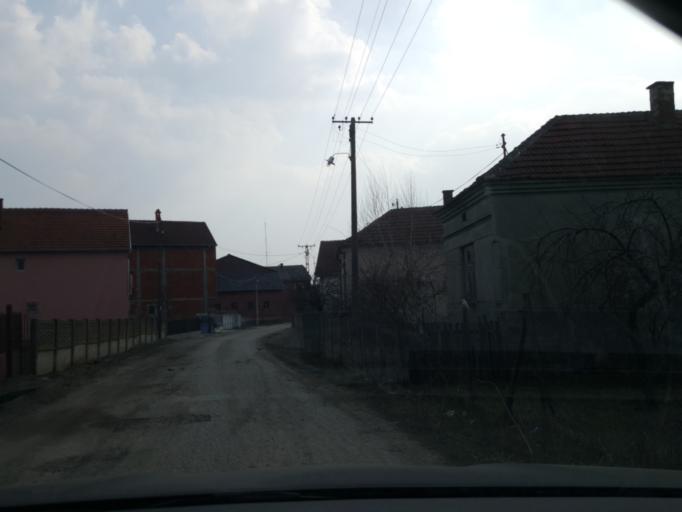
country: RS
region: Central Serbia
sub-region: Nisavski Okrug
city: Aleksinac
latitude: 43.4513
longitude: 21.7905
